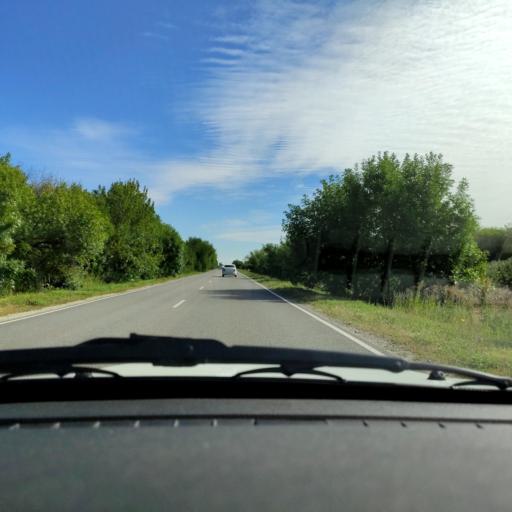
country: RU
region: Voronezj
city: Volya
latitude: 51.7050
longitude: 39.5211
